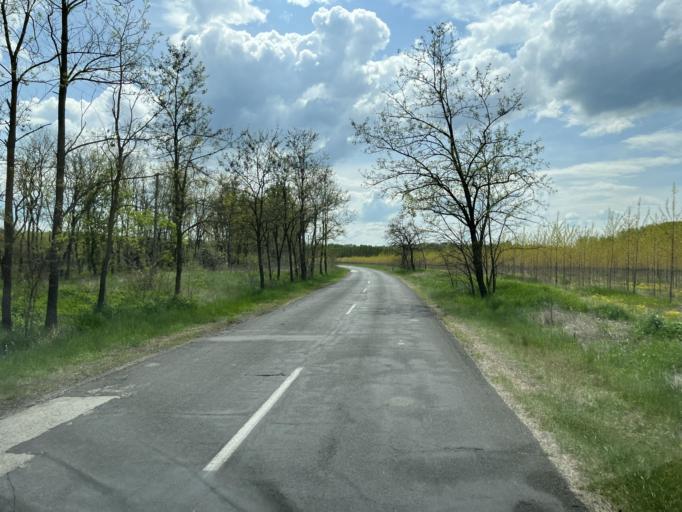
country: HU
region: Pest
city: Csemo
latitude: 47.1248
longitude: 19.6544
